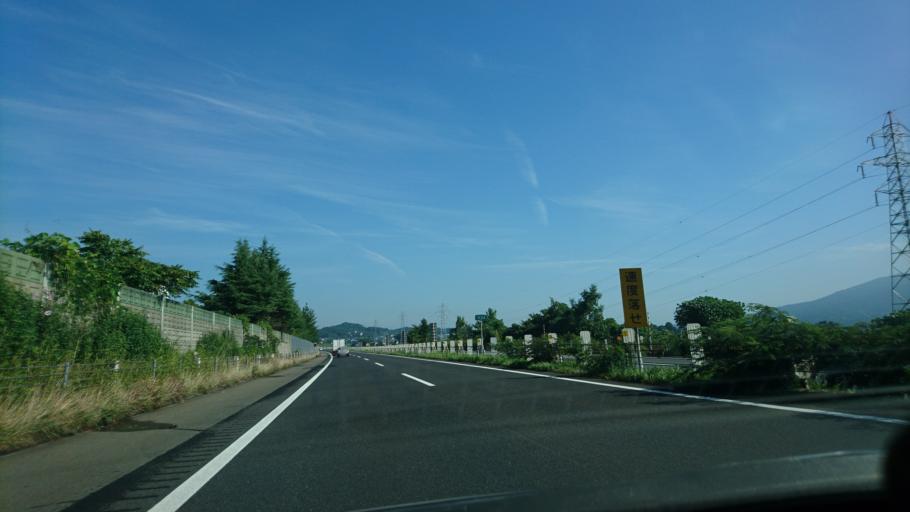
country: JP
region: Iwate
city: Ichinoseki
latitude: 38.9706
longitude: 141.1124
